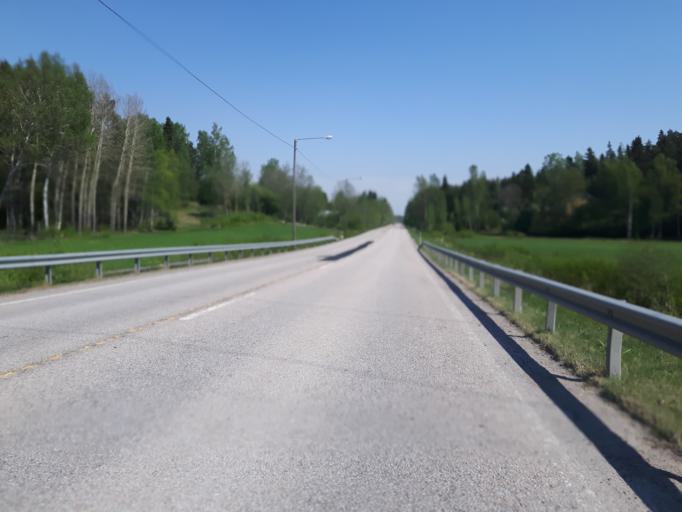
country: FI
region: Uusimaa
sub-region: Helsinki
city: Nickby
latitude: 60.3023
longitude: 25.3668
